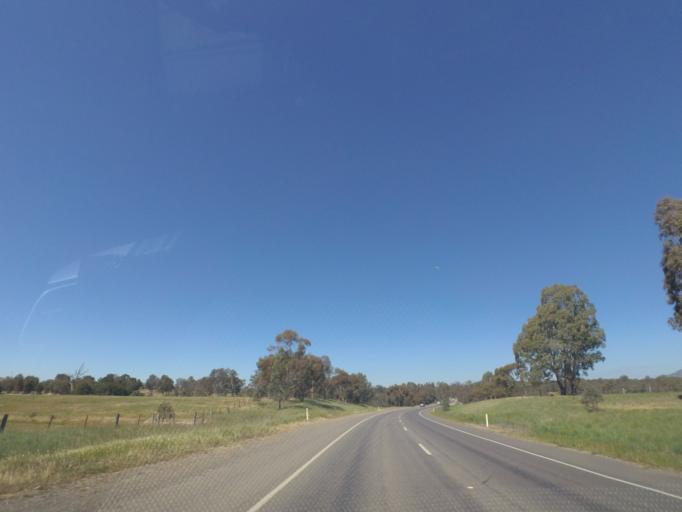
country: AU
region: Victoria
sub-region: Murrindindi
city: Kinglake West
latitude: -37.0292
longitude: 145.0919
